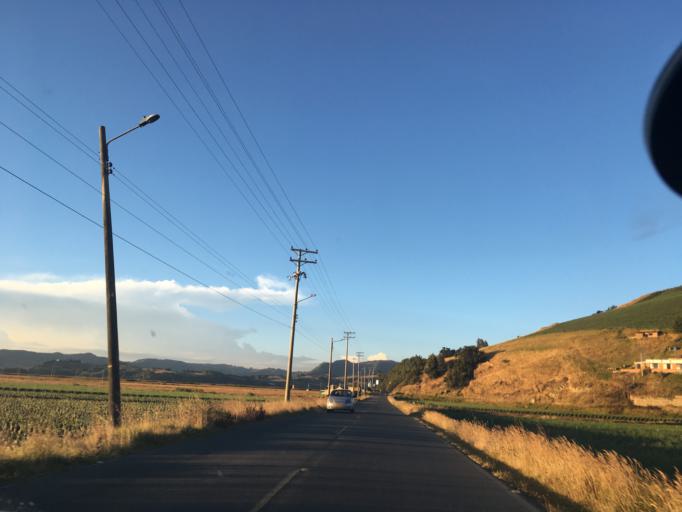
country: CO
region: Boyaca
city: Aquitania
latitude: 5.5340
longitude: -72.8846
